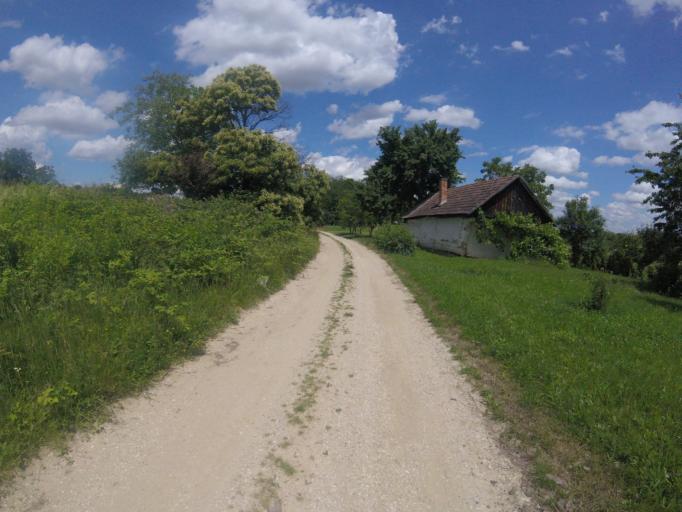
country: HU
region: Zala
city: Zalalovo
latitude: 46.8317
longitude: 16.5598
